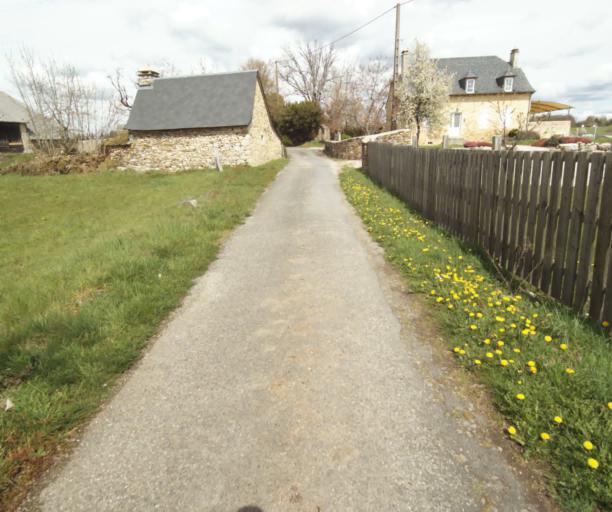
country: FR
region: Limousin
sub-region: Departement de la Correze
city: Sainte-Fortunade
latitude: 45.1963
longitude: 1.8825
